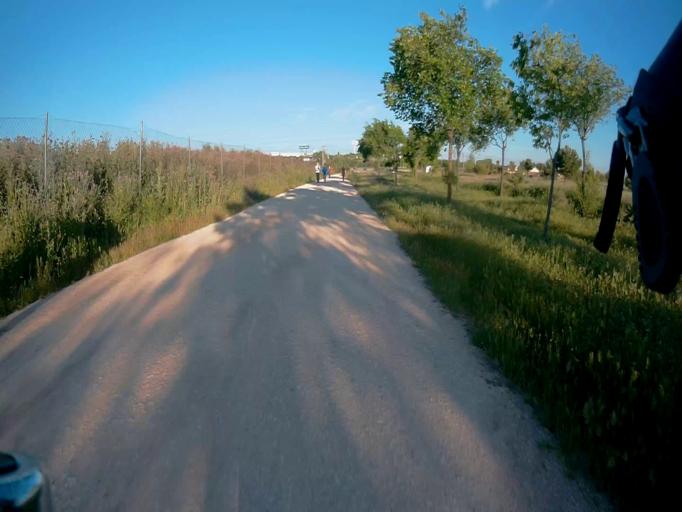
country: ES
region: Madrid
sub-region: Provincia de Madrid
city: Fuenlabrada
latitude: 40.3072
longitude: -3.7882
